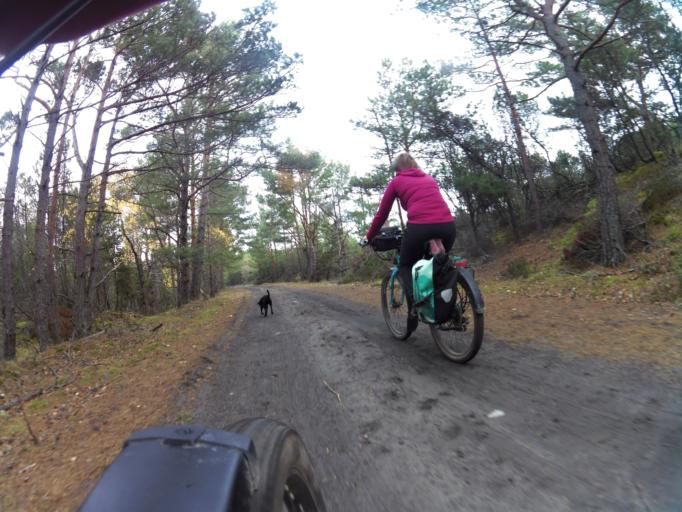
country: PL
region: Pomeranian Voivodeship
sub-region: Powiat pucki
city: Hel
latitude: 54.6192
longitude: 18.8195
